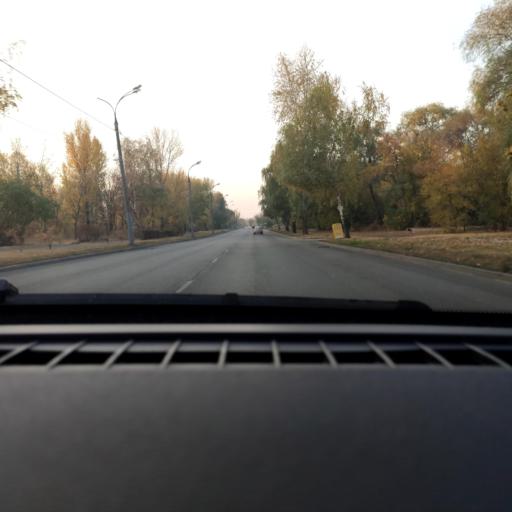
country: RU
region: Voronezj
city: Voronezh
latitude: 51.6448
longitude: 39.2110
